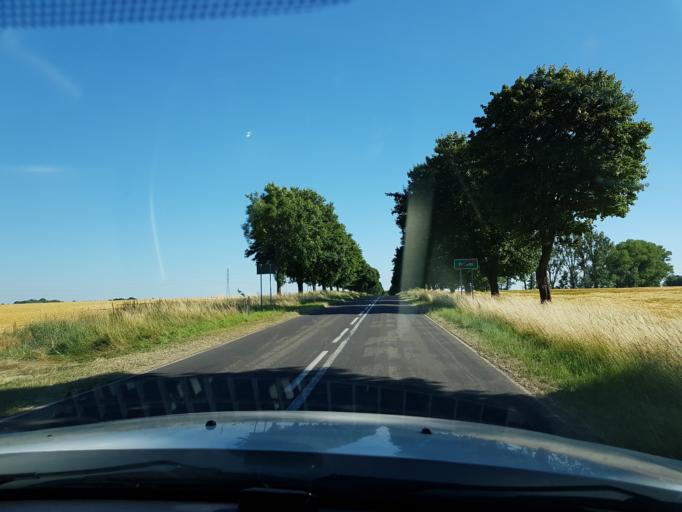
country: PL
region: West Pomeranian Voivodeship
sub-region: Powiat lobeski
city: Lobez
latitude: 53.6977
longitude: 15.6066
